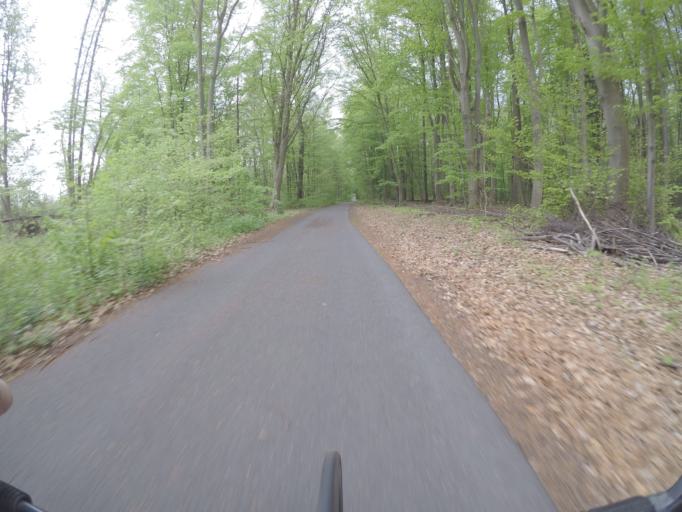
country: DE
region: Brandenburg
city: Marienwerder
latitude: 52.8588
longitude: 13.6126
